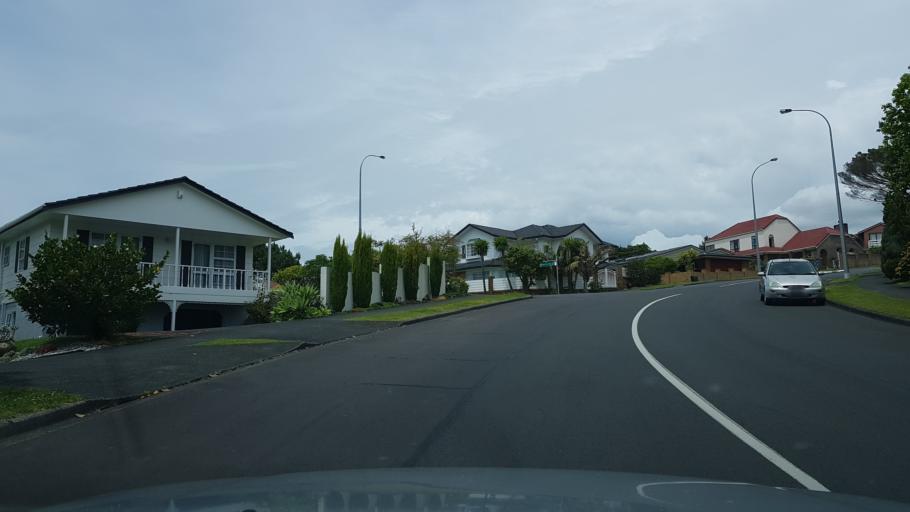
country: NZ
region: Auckland
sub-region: Auckland
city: North Shore
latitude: -36.8204
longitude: 174.7116
